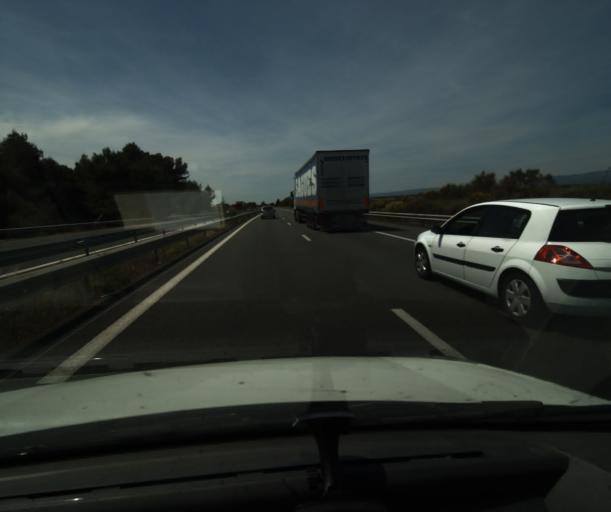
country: FR
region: Languedoc-Roussillon
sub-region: Departement de l'Aude
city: Capendu
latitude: 43.1791
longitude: 2.5334
